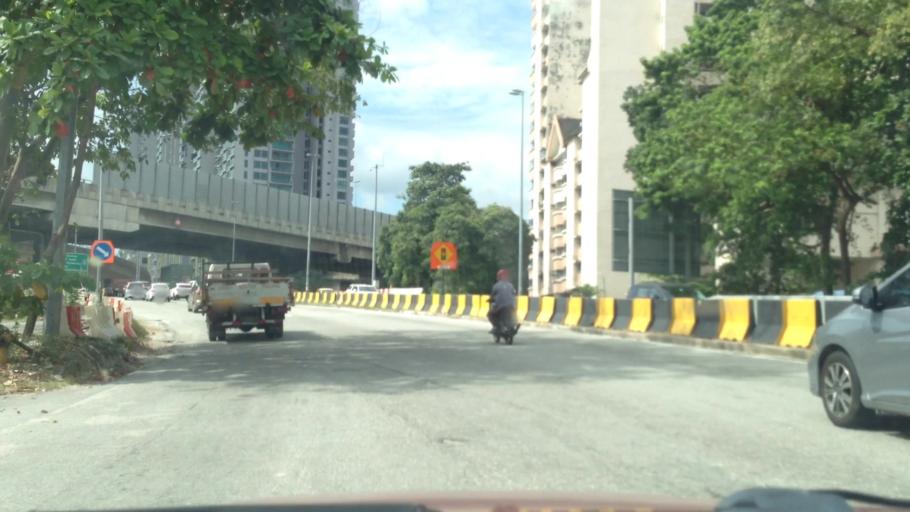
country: MY
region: Kuala Lumpur
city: Kuala Lumpur
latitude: 3.0878
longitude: 101.6933
